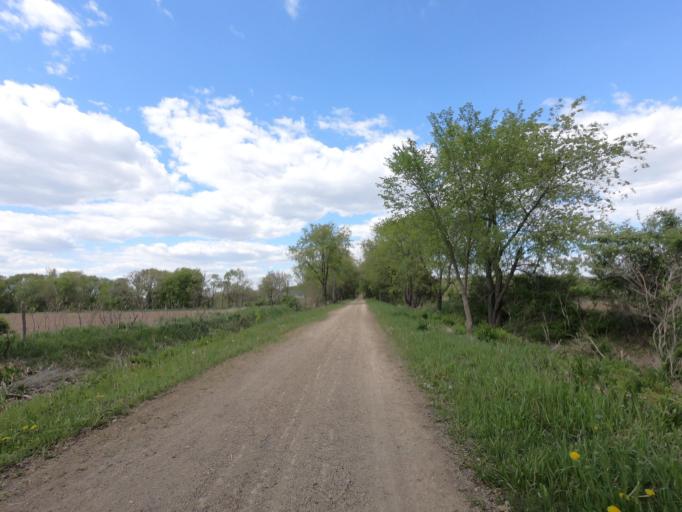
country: US
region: Wisconsin
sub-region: Dane County
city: Belleville
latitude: 42.8804
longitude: -89.5289
